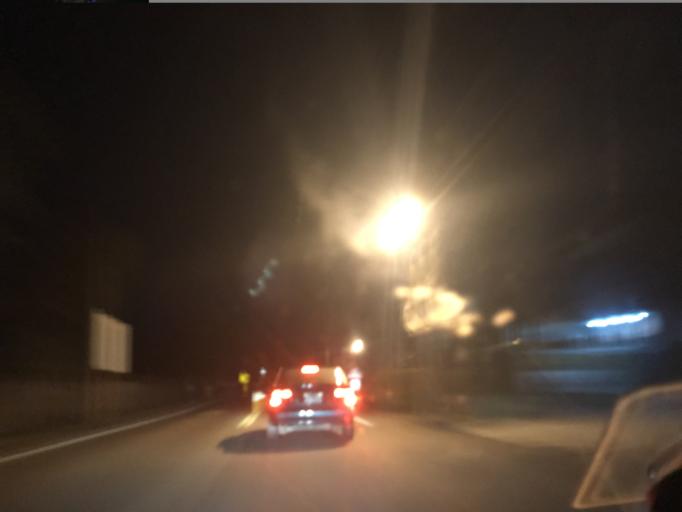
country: TW
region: Taiwan
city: Daxi
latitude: 24.8346
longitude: 121.2038
